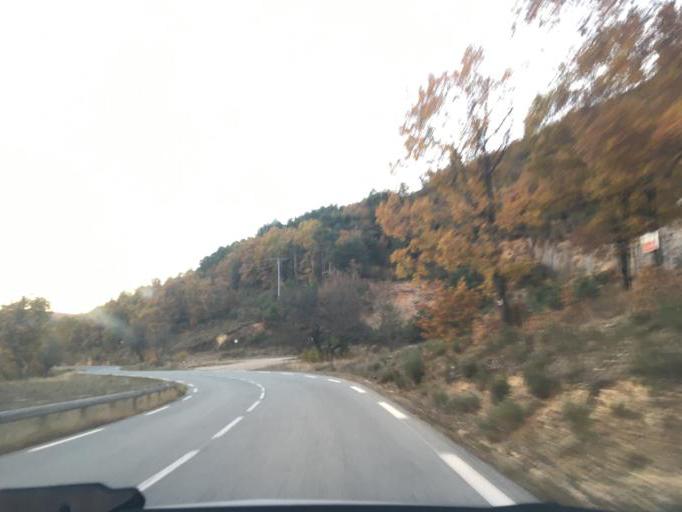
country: FR
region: Provence-Alpes-Cote d'Azur
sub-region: Departement du Var
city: Bargemon
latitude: 43.6870
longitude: 6.5090
